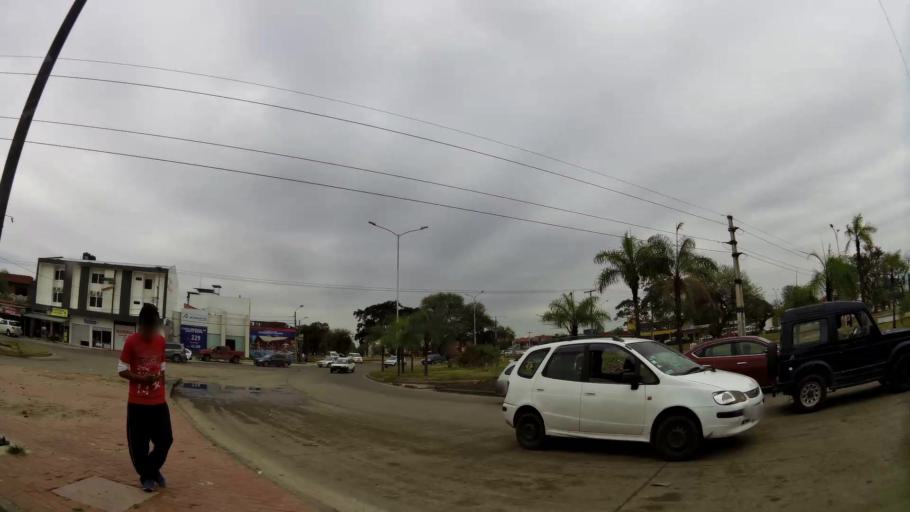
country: BO
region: Santa Cruz
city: Santa Cruz de la Sierra
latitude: -17.7515
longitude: -63.1914
